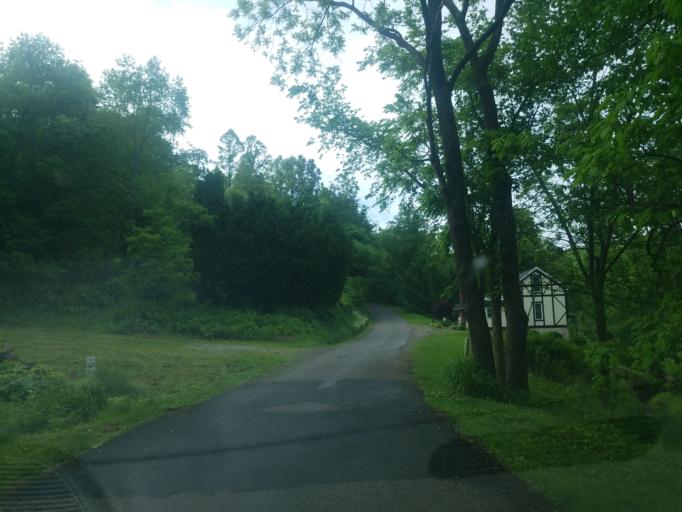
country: US
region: Ohio
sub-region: Holmes County
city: Millersburg
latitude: 40.5266
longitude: -81.8914
